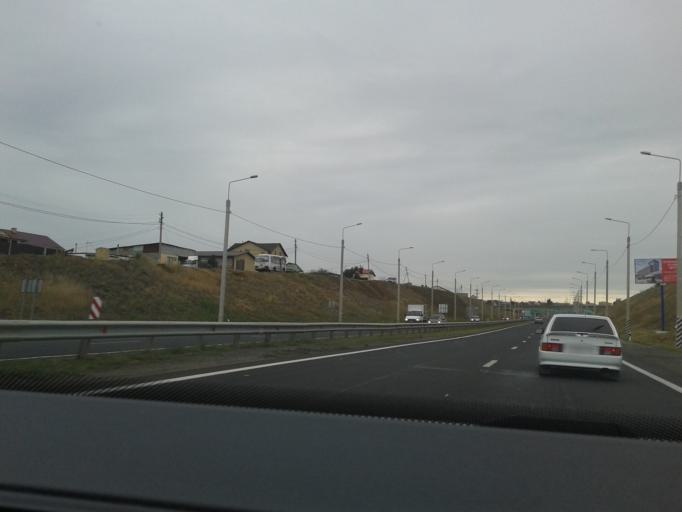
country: RU
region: Volgograd
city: Gorodishche
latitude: 48.7961
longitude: 44.4570
